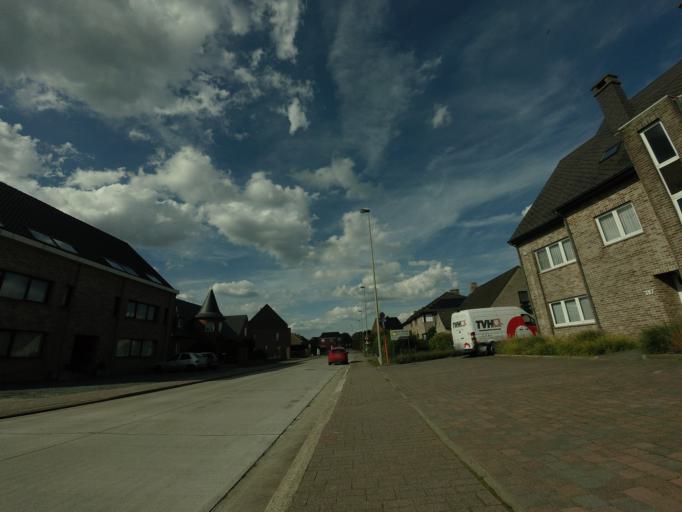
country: BE
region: Flanders
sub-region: Provincie Vlaams-Brabant
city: Meise
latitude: 50.9598
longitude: 4.3442
